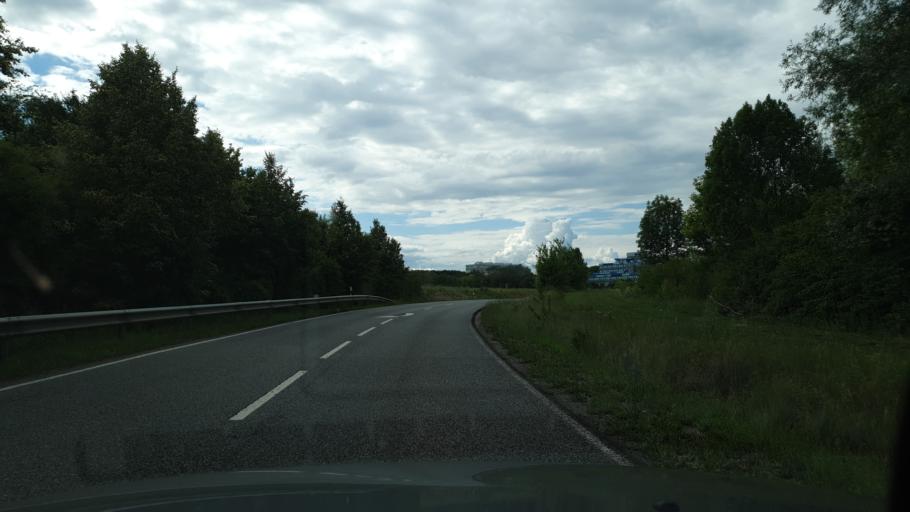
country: DE
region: Rheinland-Pfalz
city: Klein-Winternheim
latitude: 49.9538
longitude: 8.2066
